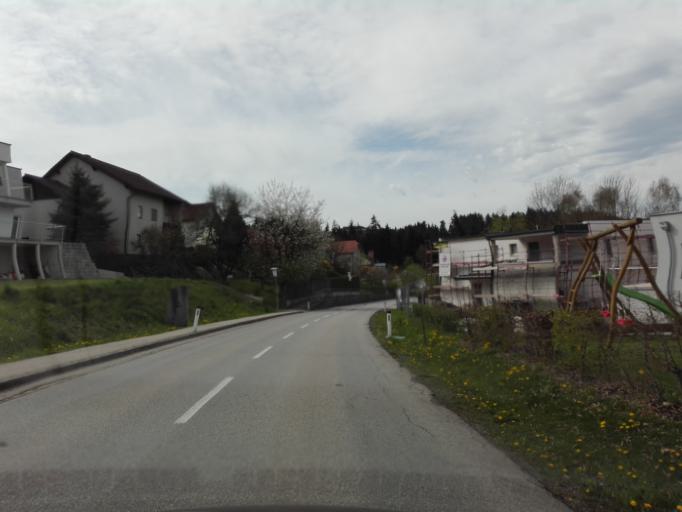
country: AT
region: Upper Austria
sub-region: Politischer Bezirk Urfahr-Umgebung
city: Gramastetten
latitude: 48.3775
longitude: 14.1925
